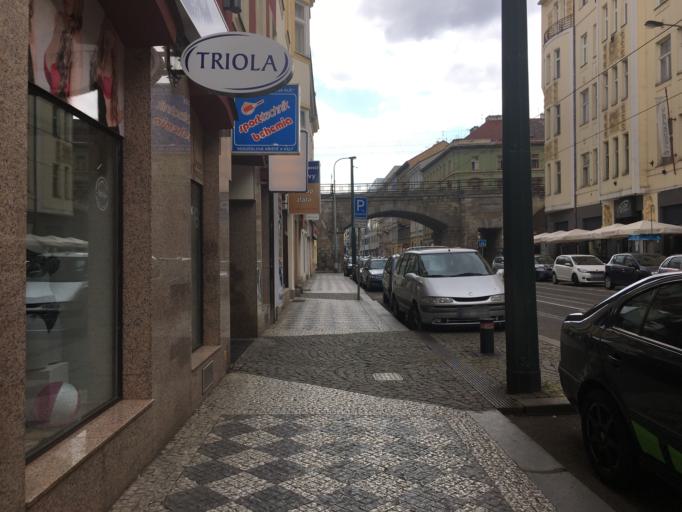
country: CZ
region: Praha
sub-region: Praha 8
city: Karlin
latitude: 50.0922
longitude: 14.4430
